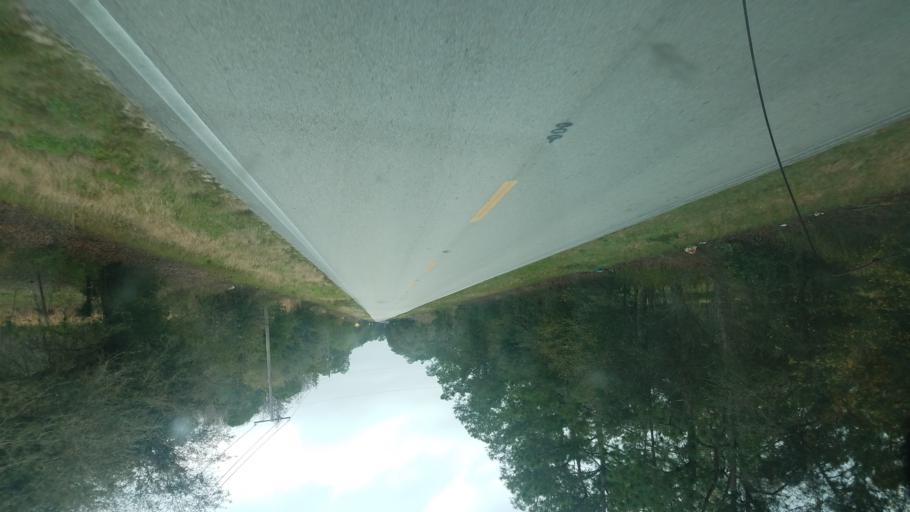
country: US
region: Florida
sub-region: Polk County
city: Gibsonia
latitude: 28.2590
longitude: -81.9497
